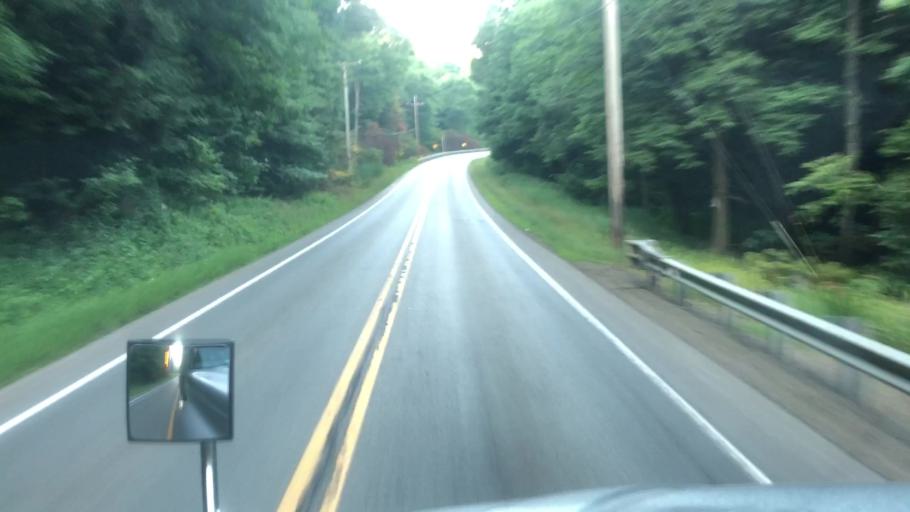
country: US
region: Pennsylvania
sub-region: Venango County
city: Hasson Heights
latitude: 41.4820
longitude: -79.6573
